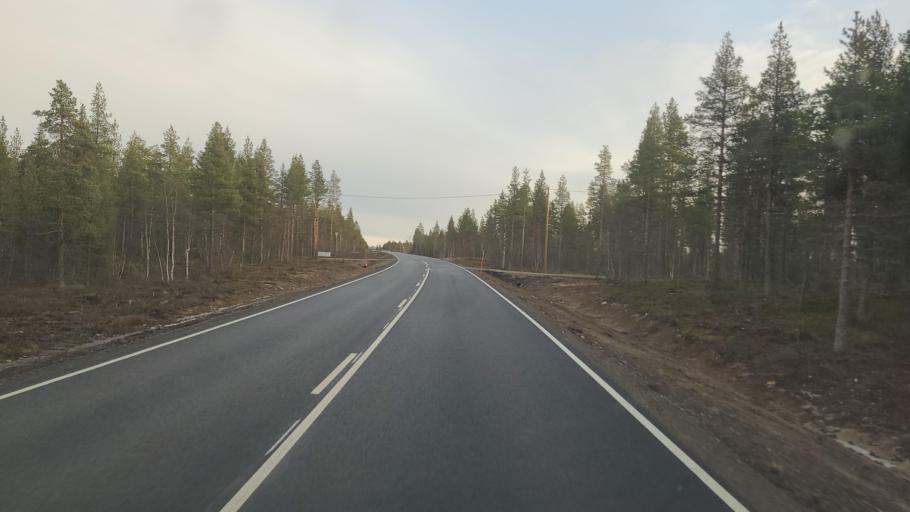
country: FI
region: Lapland
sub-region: Tunturi-Lappi
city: Kittilae
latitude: 67.8721
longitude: 24.9001
